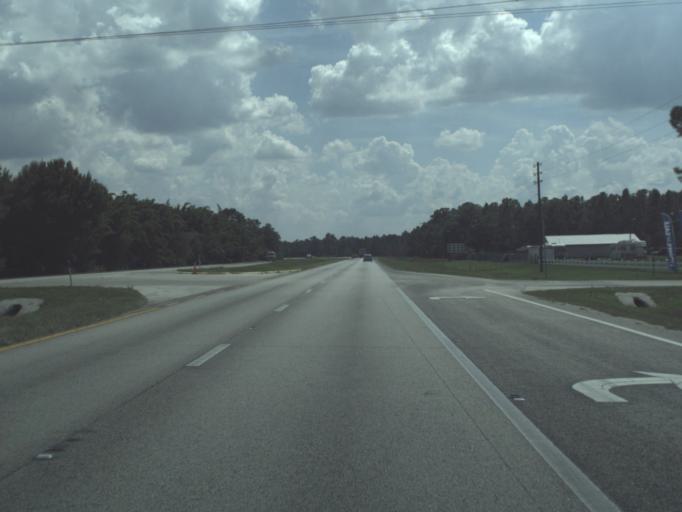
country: US
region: Florida
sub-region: Polk County
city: Crooked Lake Park
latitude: 27.7764
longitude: -81.5974
